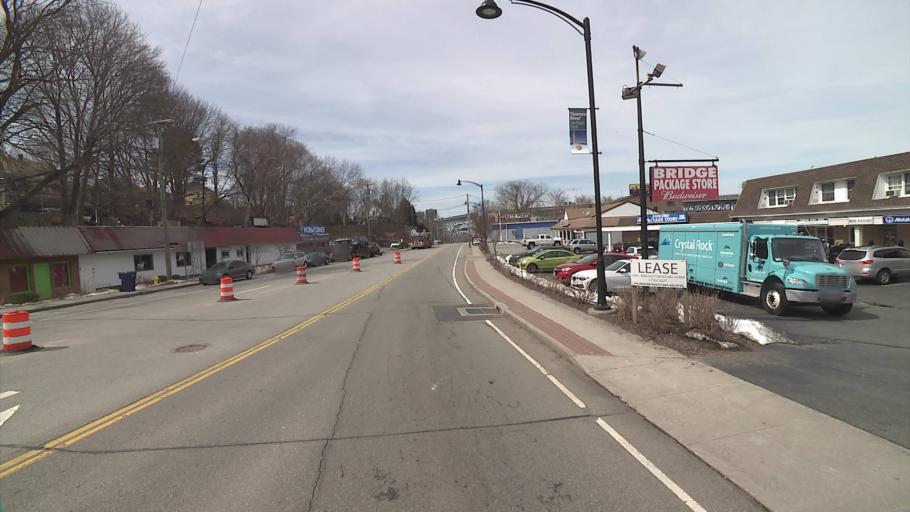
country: US
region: Connecticut
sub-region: New London County
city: Groton
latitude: 41.3618
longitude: -72.0785
